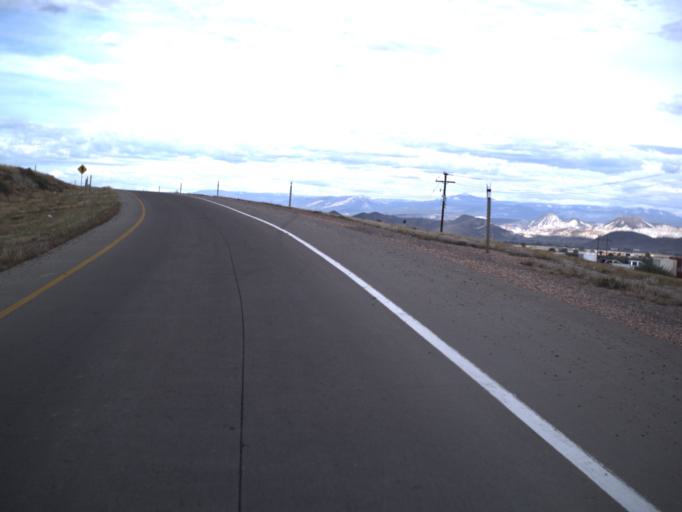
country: US
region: Utah
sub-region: Sevier County
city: Richfield
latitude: 38.7906
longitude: -112.0798
